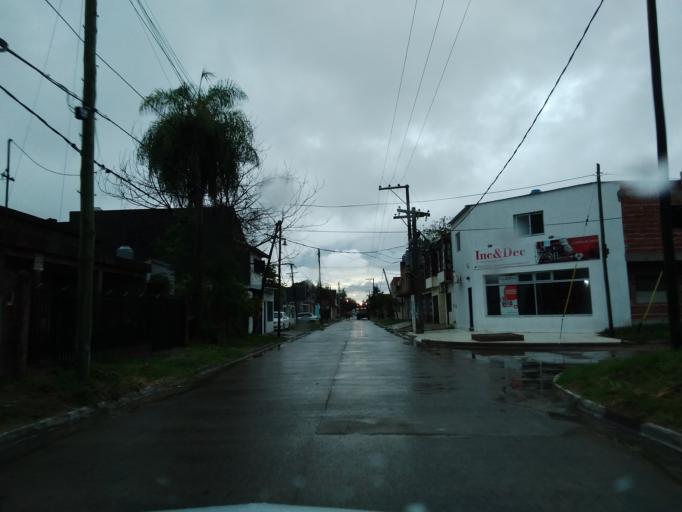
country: AR
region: Corrientes
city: Corrientes
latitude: -27.4966
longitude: -58.8208
